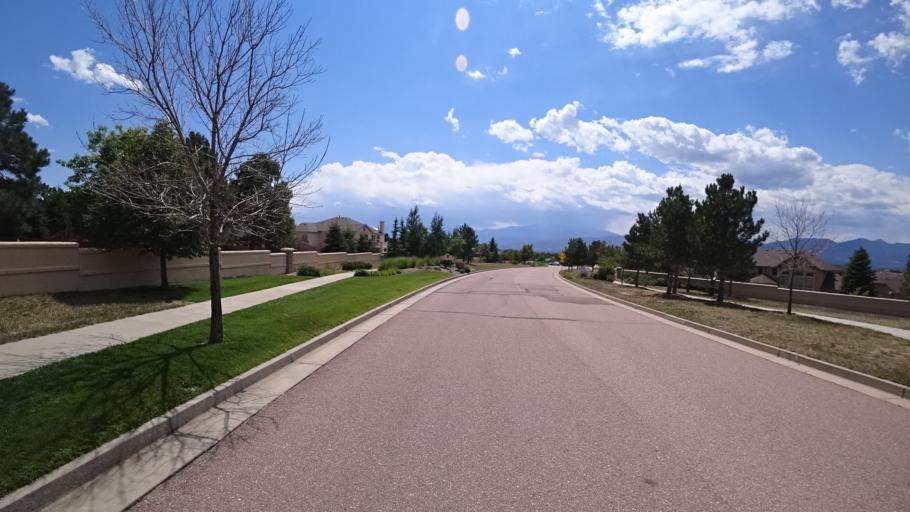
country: US
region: Colorado
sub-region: El Paso County
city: Black Forest
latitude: 38.9706
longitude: -104.7583
